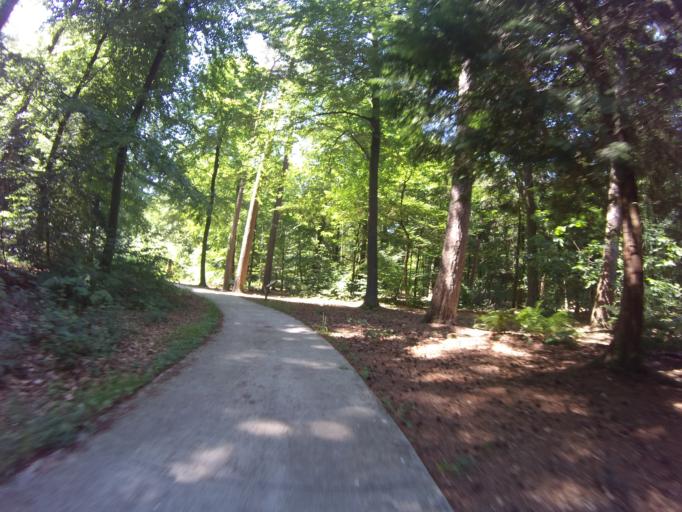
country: NL
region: Drenthe
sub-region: Gemeente Emmen
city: Emmen
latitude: 52.7893
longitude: 6.9177
